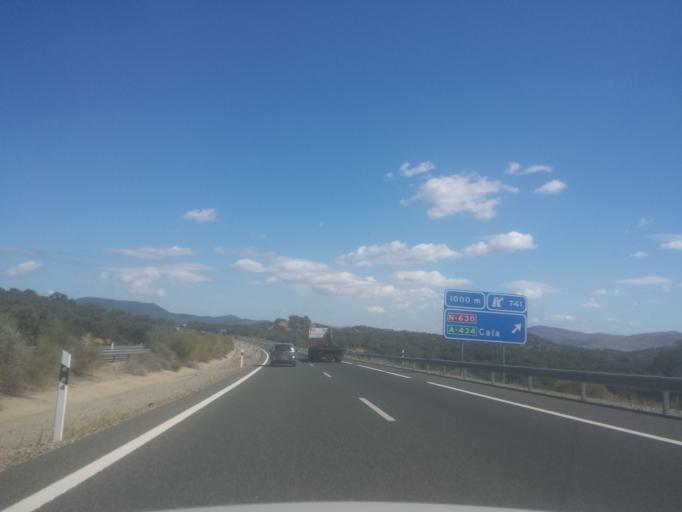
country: ES
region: Andalusia
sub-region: Provincia de Huelva
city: Santa Olalla del Cala
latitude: 37.9380
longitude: -6.2265
